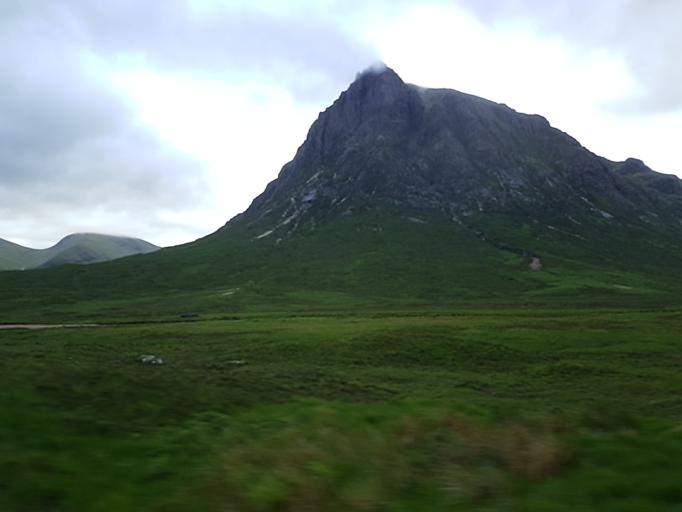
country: GB
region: Scotland
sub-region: Highland
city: Spean Bridge
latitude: 56.6580
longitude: -4.8796
